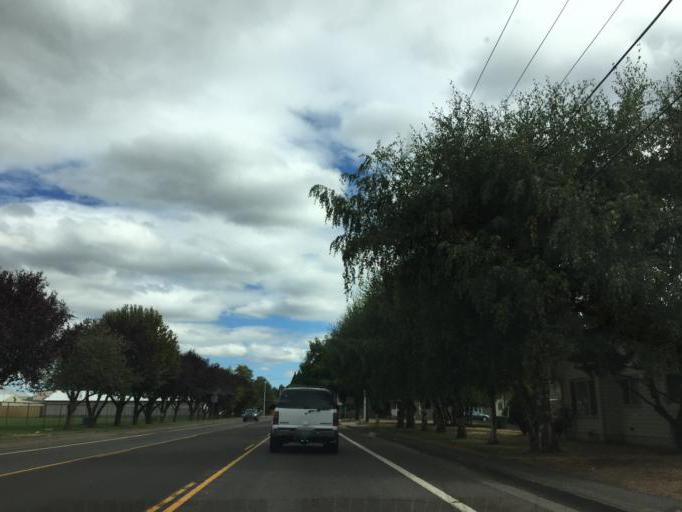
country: US
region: Oregon
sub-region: Marion County
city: Woodburn
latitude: 45.1496
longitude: -122.8635
